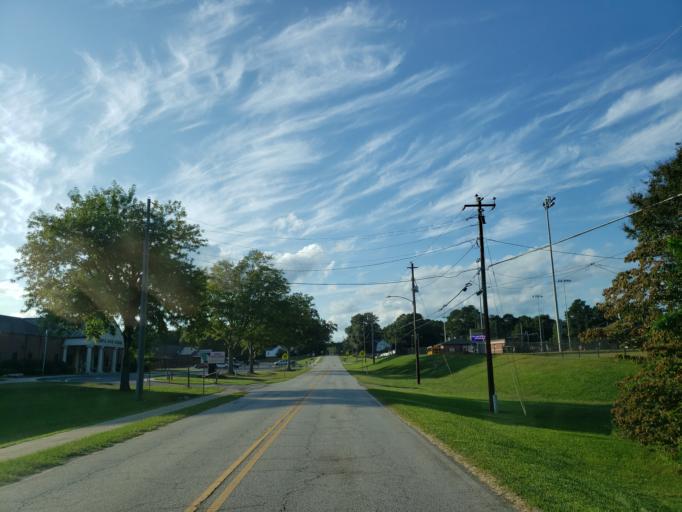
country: US
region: Georgia
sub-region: Carroll County
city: Temple
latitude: 33.7322
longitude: -85.0242
